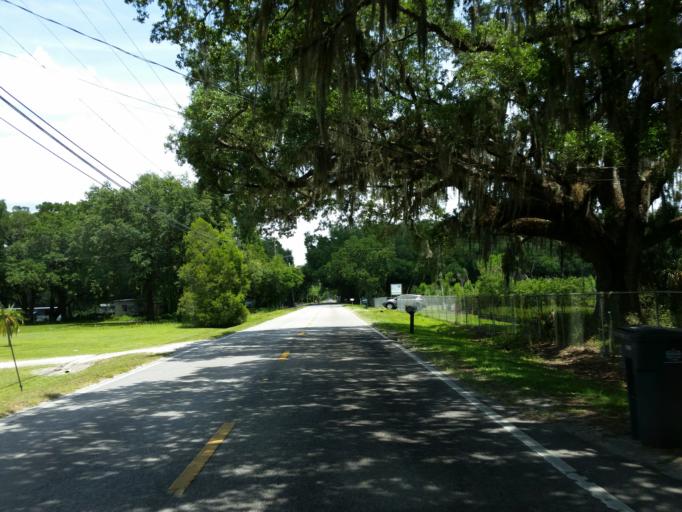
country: US
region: Florida
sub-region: Hillsborough County
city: Dover
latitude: 28.0471
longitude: -82.2132
